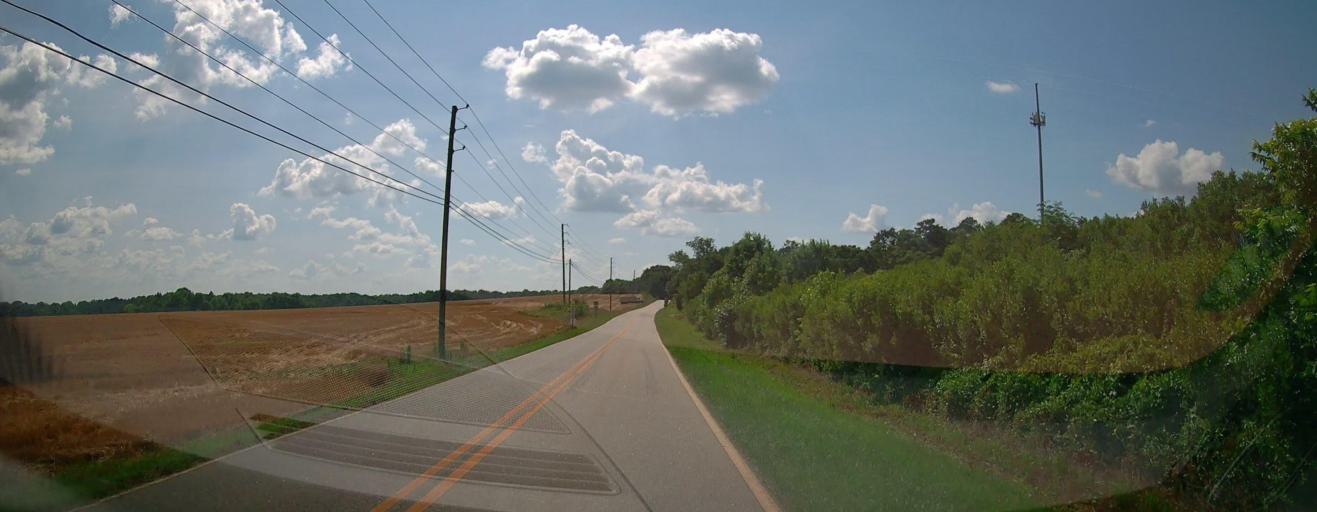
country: US
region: Georgia
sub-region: Spalding County
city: East Griffin
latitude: 33.2265
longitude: -84.1219
